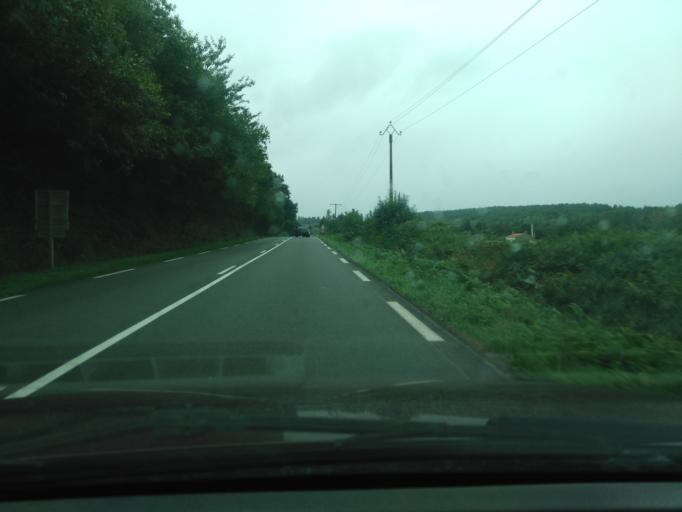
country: FR
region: Pays de la Loire
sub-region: Departement de la Vendee
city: Sainte-Hermine
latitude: 46.5837
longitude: -1.1141
